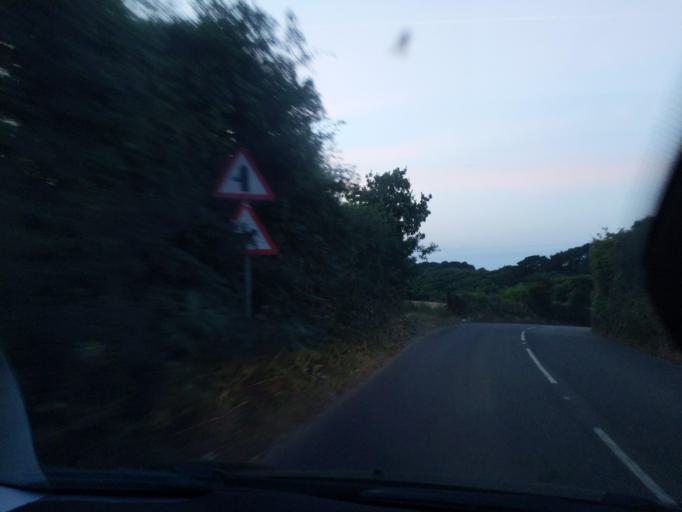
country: GB
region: England
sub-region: Cornwall
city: Camborne
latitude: 50.1900
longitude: -5.3072
